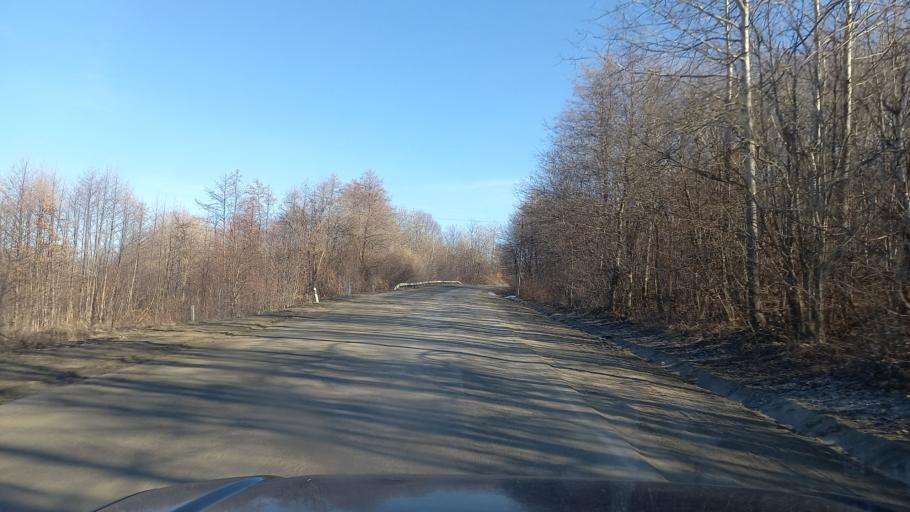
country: RU
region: Adygeya
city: Kamennomostskiy
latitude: 44.2785
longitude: 40.2409
